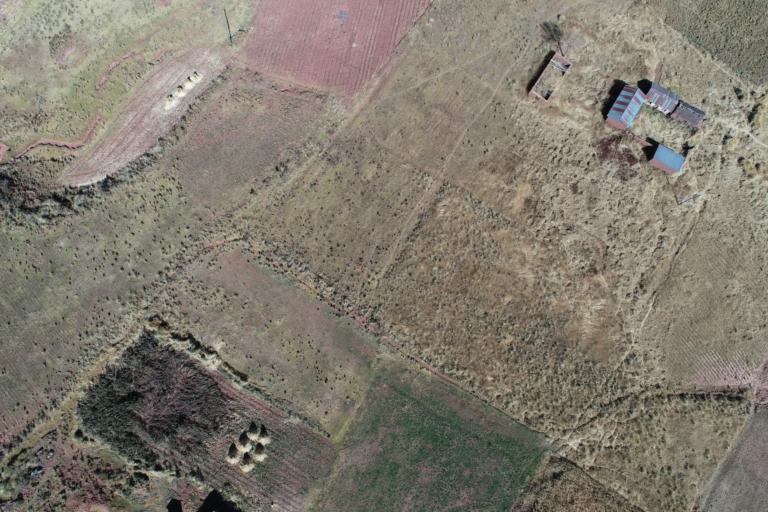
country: BO
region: La Paz
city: Tiahuanaco
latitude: -16.5951
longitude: -68.7602
